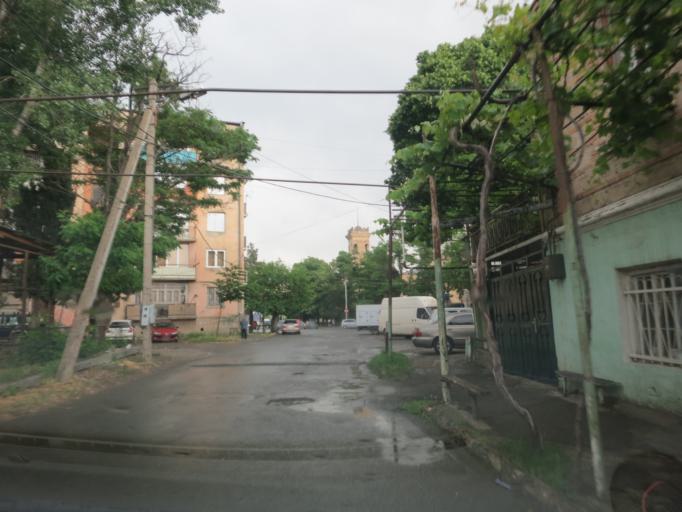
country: GE
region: Shida Kartli
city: Gori
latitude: 41.9882
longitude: 44.1123
